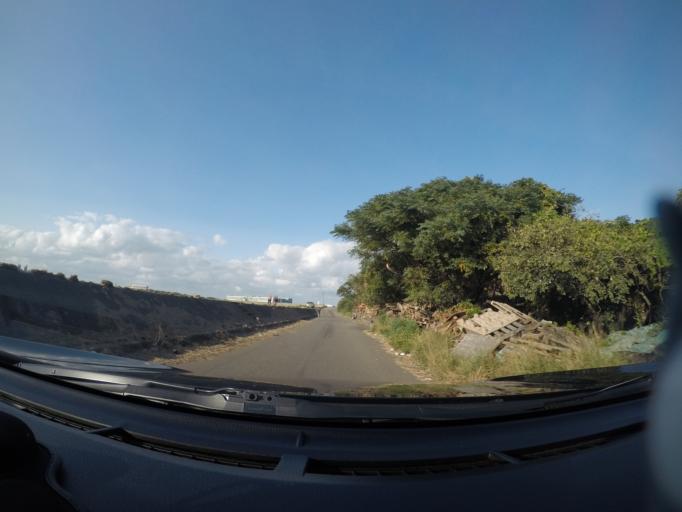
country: TW
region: Taiwan
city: Taoyuan City
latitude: 25.1006
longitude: 121.2517
